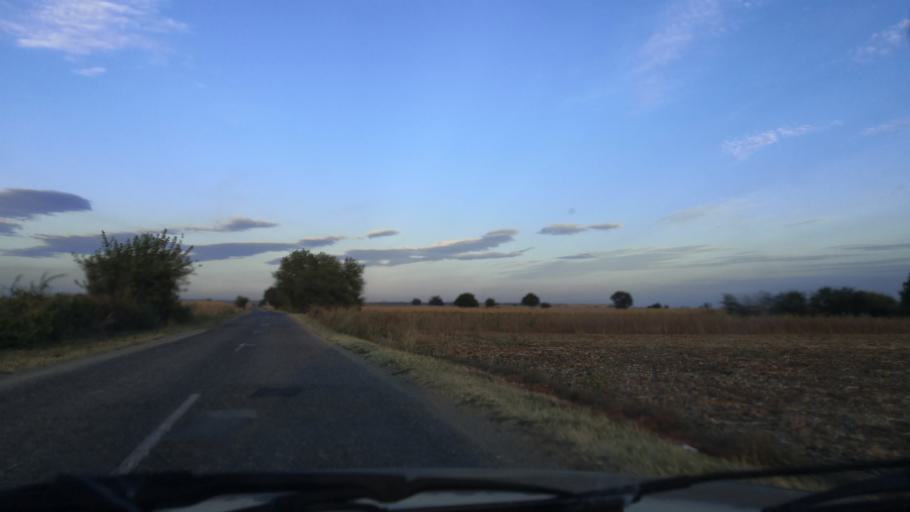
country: RO
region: Mehedinti
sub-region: Comuna Gruia
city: Izvoarele
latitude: 44.2530
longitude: 22.6171
